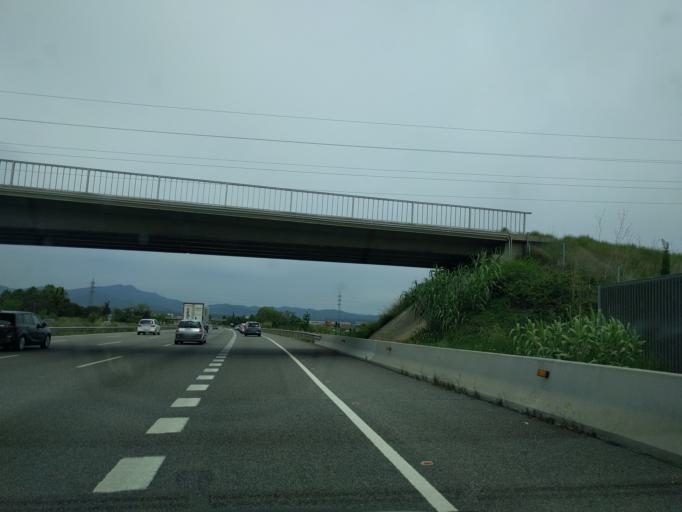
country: ES
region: Catalonia
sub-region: Provincia de Girona
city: Vilablareix
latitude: 41.9554
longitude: 2.7860
